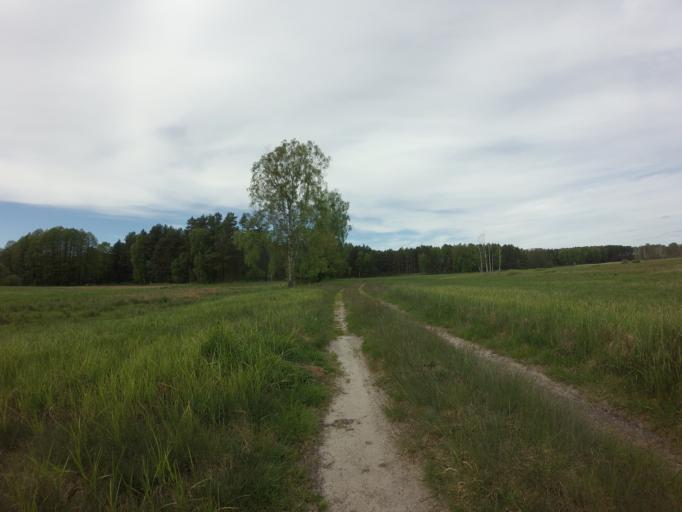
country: PL
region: West Pomeranian Voivodeship
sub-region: Powiat choszczenski
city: Drawno
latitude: 53.1624
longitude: 15.6658
